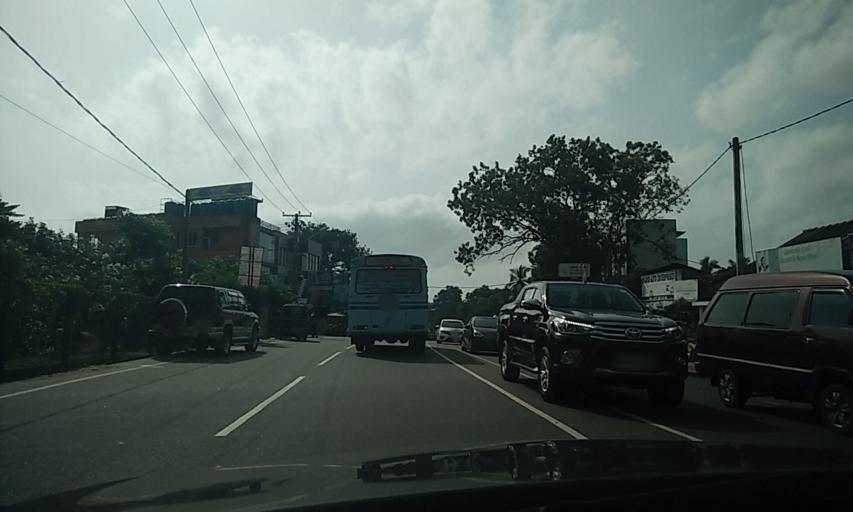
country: LK
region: Western
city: Maharagama
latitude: 6.8598
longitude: 79.9066
